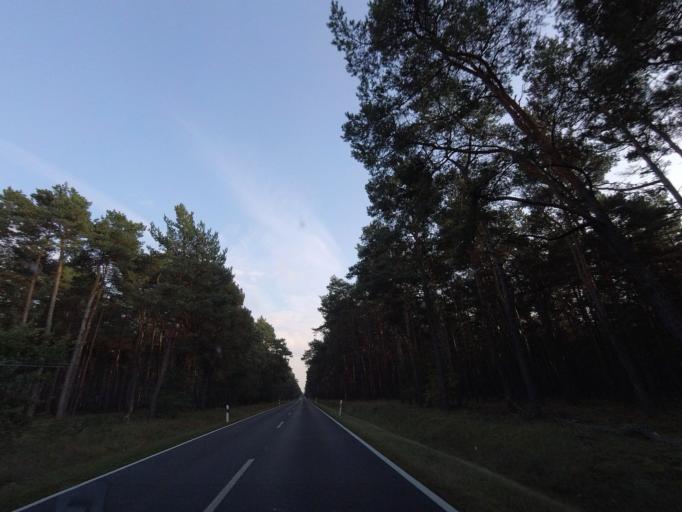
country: DE
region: Brandenburg
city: Bruck
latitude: 52.1738
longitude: 12.7613
